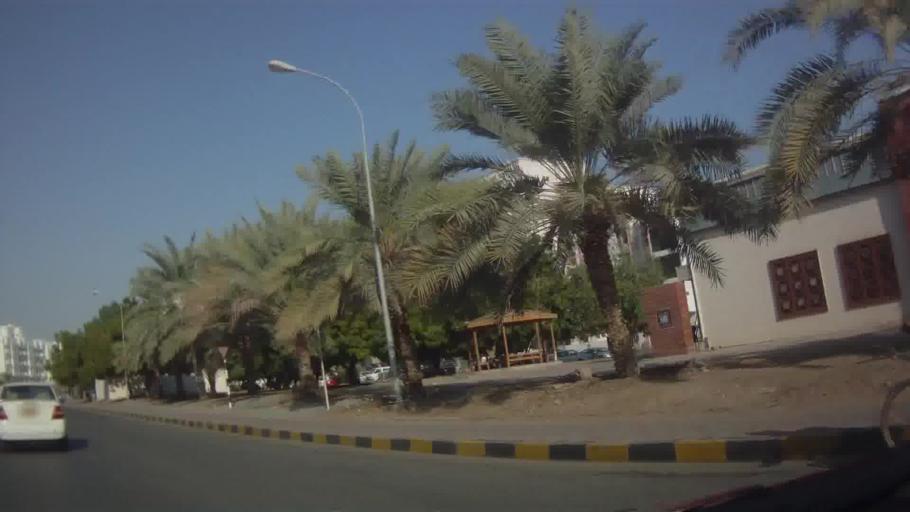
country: OM
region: Muhafazat Masqat
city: Bawshar
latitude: 23.5865
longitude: 58.4251
